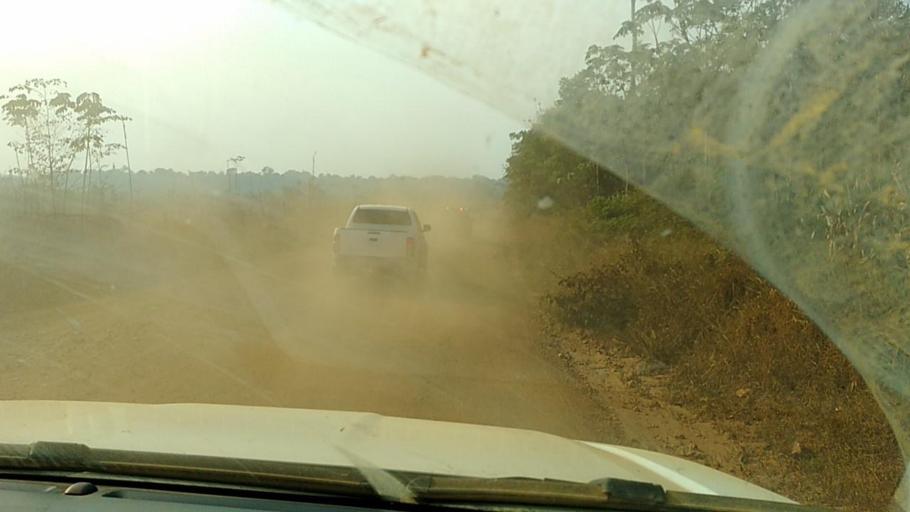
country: BR
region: Rondonia
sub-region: Porto Velho
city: Porto Velho
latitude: -8.7415
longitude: -63.9657
